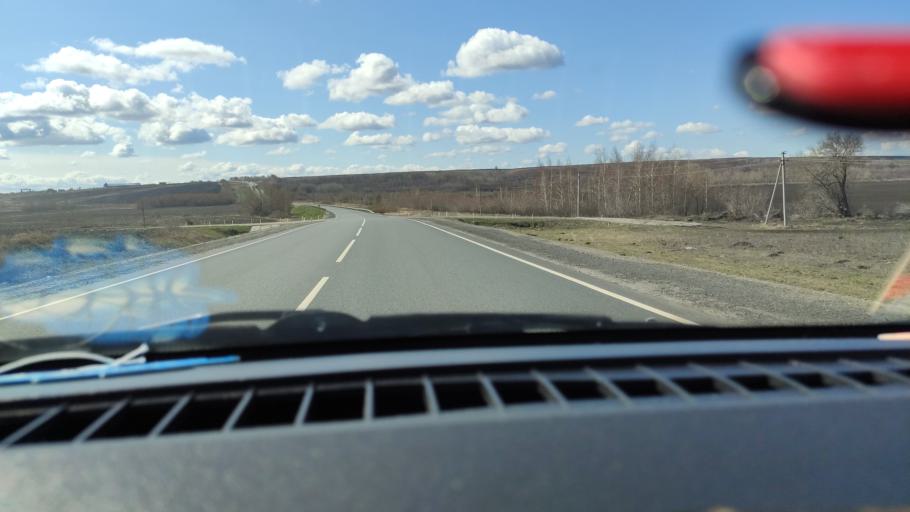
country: RU
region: Samara
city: Syzran'
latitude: 52.9705
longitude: 48.3083
